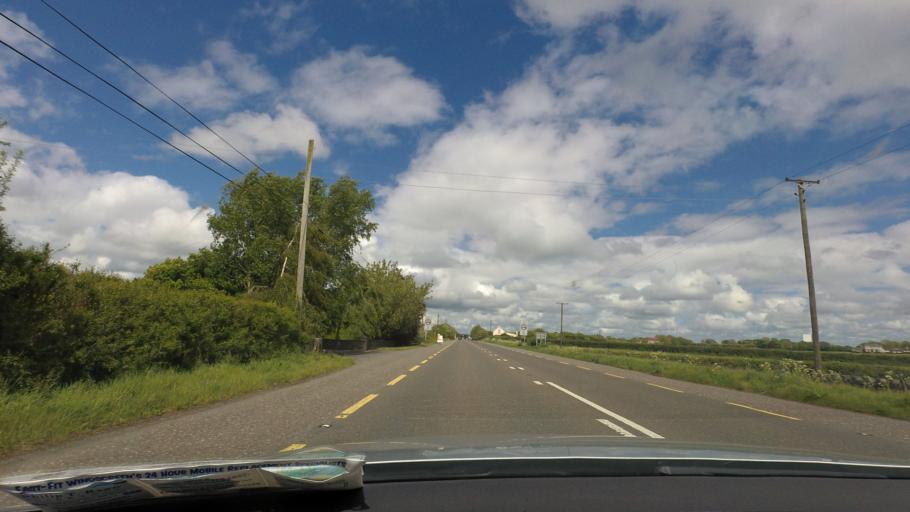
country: IE
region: Munster
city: Thurles
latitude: 52.6120
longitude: -7.7812
